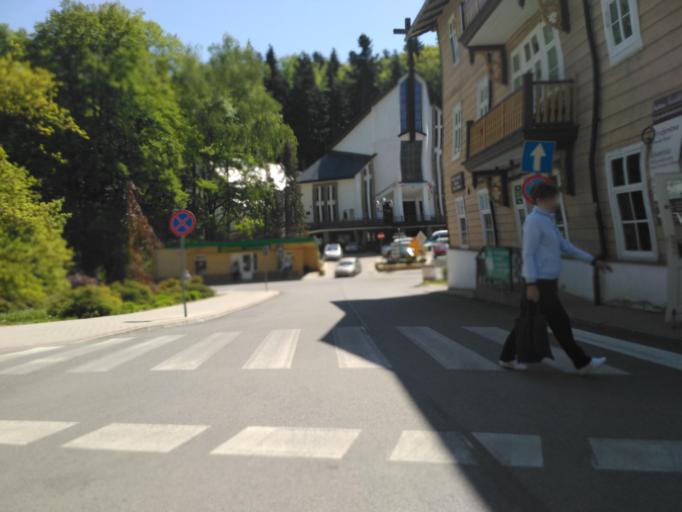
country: PL
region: Subcarpathian Voivodeship
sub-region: Powiat krosnienski
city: Iwonicz-Zdroj
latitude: 49.5626
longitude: 21.7890
